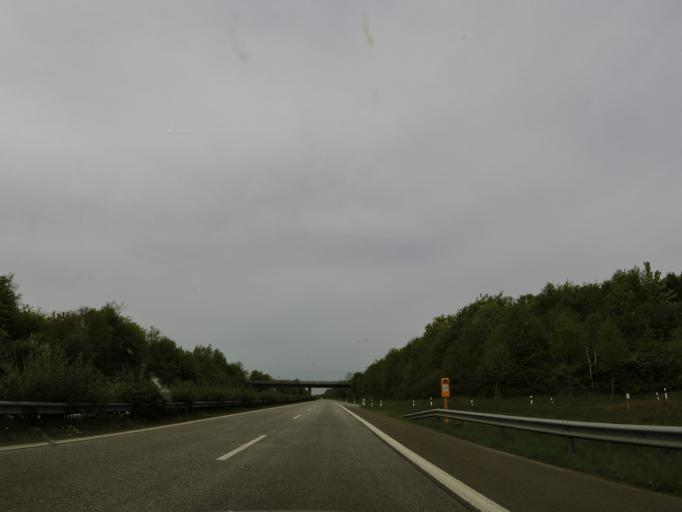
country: DE
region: Schleswig-Holstein
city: Besdorf
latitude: 54.0587
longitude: 9.3654
